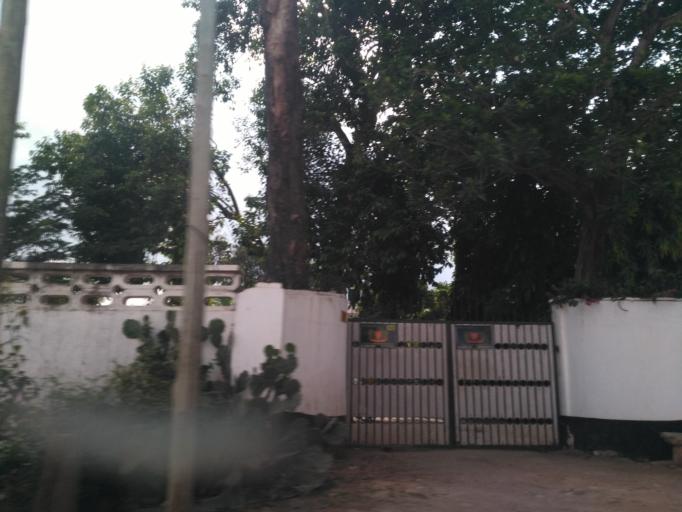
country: TZ
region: Dar es Salaam
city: Dar es Salaam
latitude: -6.8043
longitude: 39.2758
